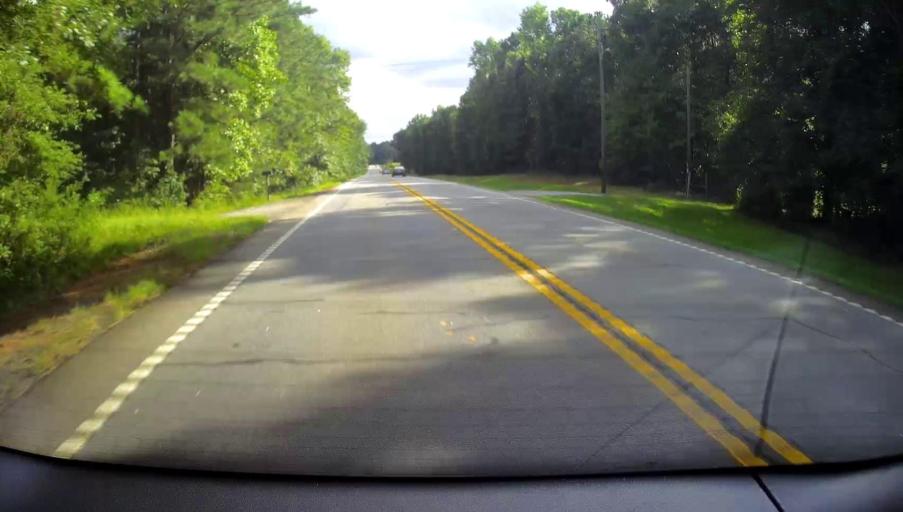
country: US
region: Georgia
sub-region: Coweta County
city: Senoia
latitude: 33.2189
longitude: -84.5777
